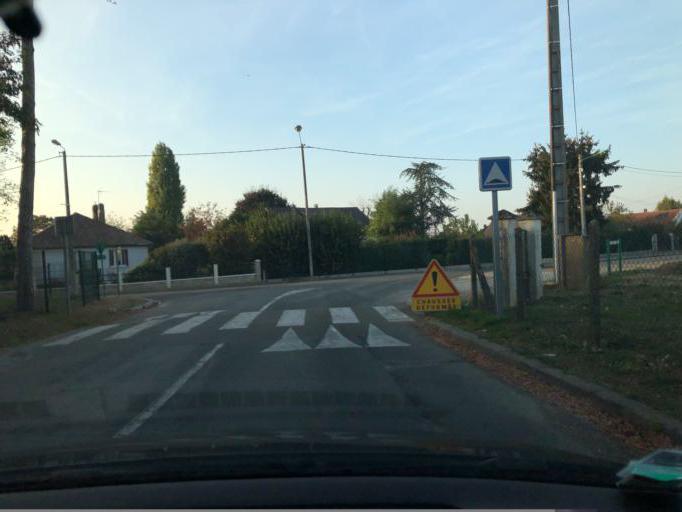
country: FR
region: Bourgogne
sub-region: Departement de l'Yonne
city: Saint-Clement
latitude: 48.2137
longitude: 3.2916
